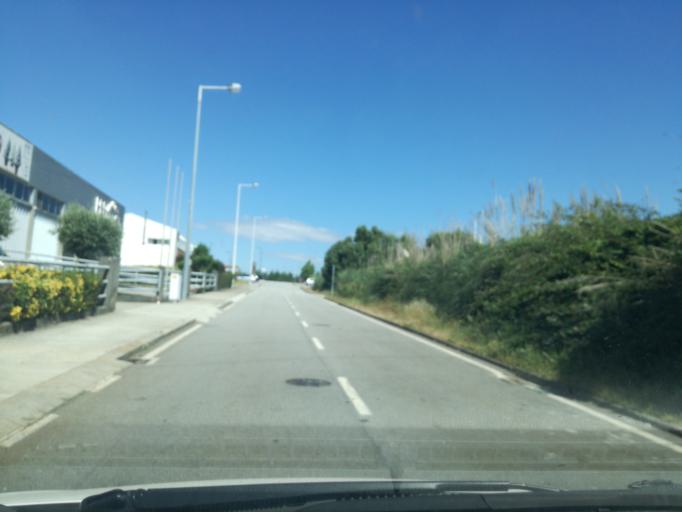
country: PT
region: Porto
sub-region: Maia
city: Gemunde
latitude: 41.2598
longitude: -8.6388
